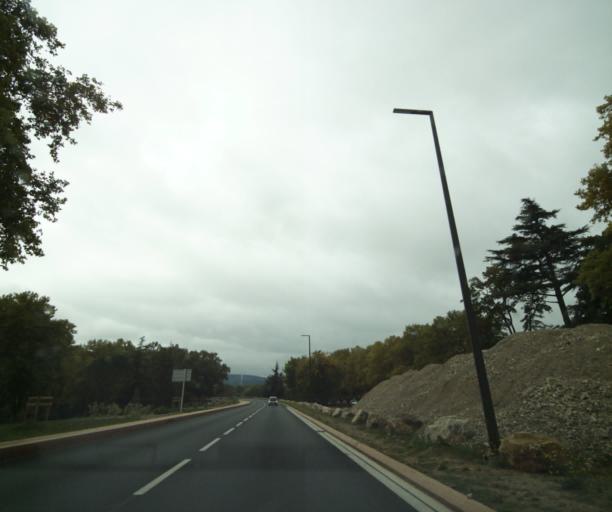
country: FR
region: Midi-Pyrenees
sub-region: Departement de l'Aveyron
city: Millau
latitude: 44.0949
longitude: 3.0846
